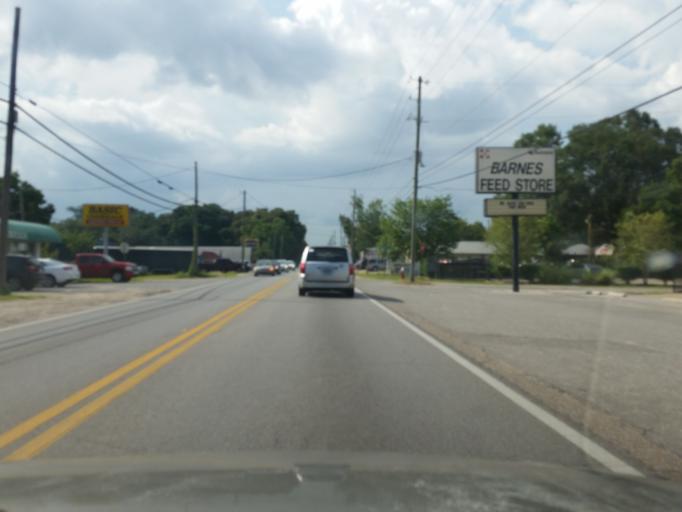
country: US
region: Florida
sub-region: Escambia County
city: Ensley
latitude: 30.5228
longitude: -87.2683
